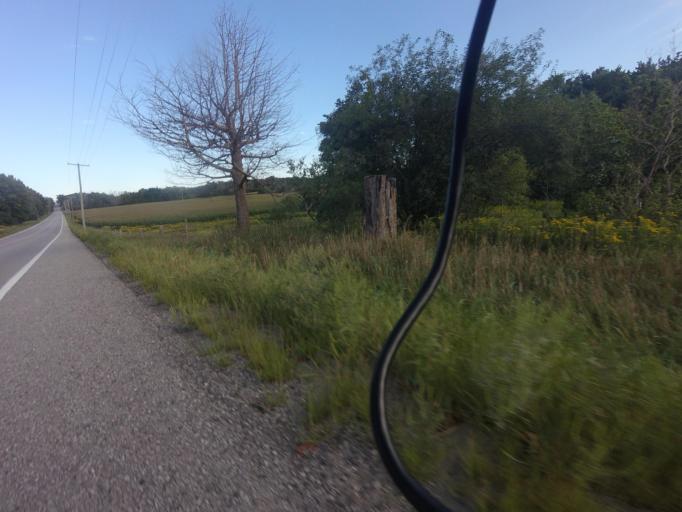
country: CA
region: Ontario
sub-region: Wellington County
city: Guelph
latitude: 43.5813
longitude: -80.3374
